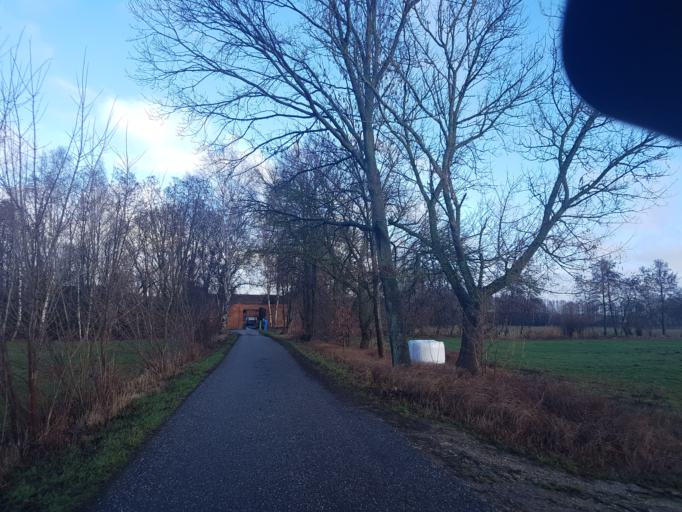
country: DE
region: Brandenburg
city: Ruckersdorf
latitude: 51.5982
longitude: 13.6246
